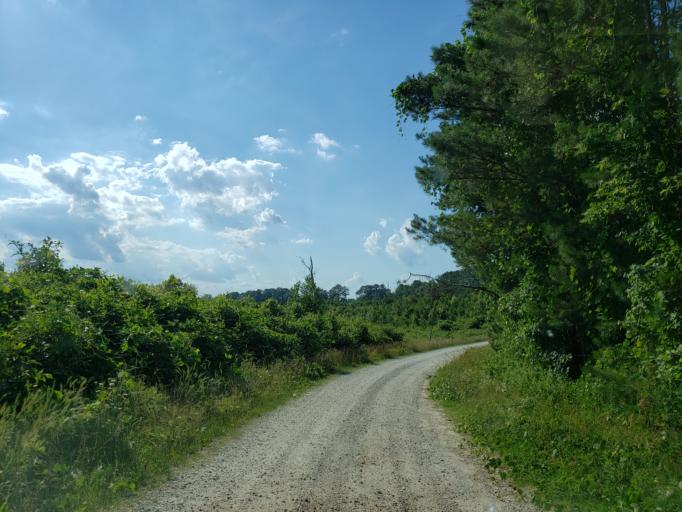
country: US
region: Georgia
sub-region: Haralson County
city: Buchanan
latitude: 33.8075
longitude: -85.1024
